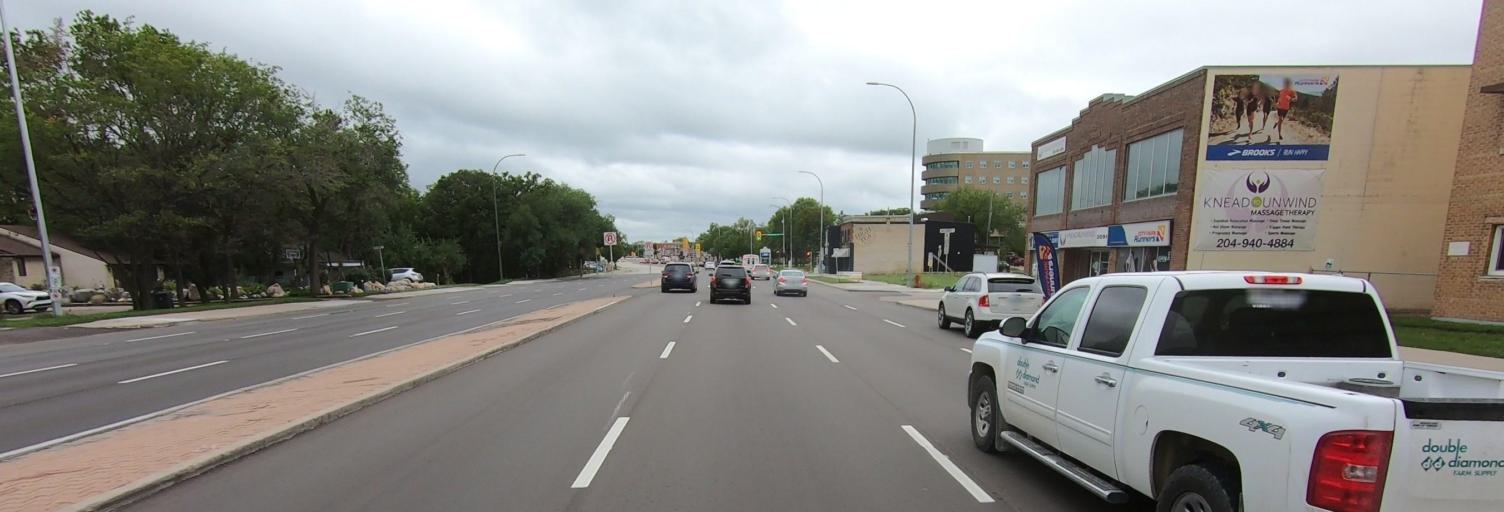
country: CA
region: Manitoba
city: Winnipeg
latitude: 49.8773
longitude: -97.2327
